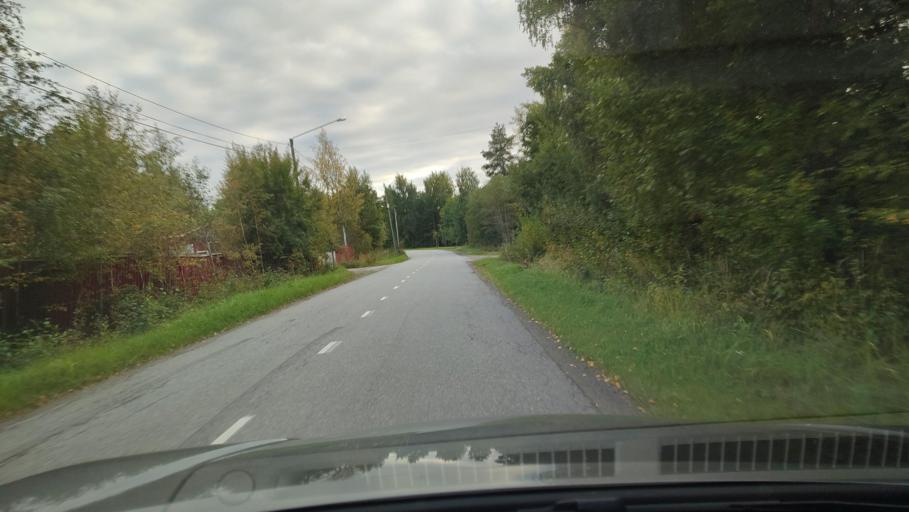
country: FI
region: Ostrobothnia
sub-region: Sydosterbotten
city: Kristinestad
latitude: 62.2606
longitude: 21.3840
